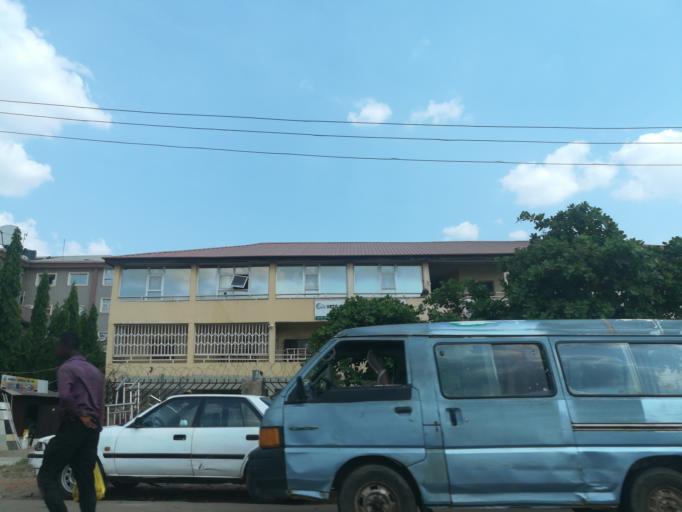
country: NG
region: Abuja Federal Capital Territory
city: Abuja
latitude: 9.0733
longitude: 7.4342
